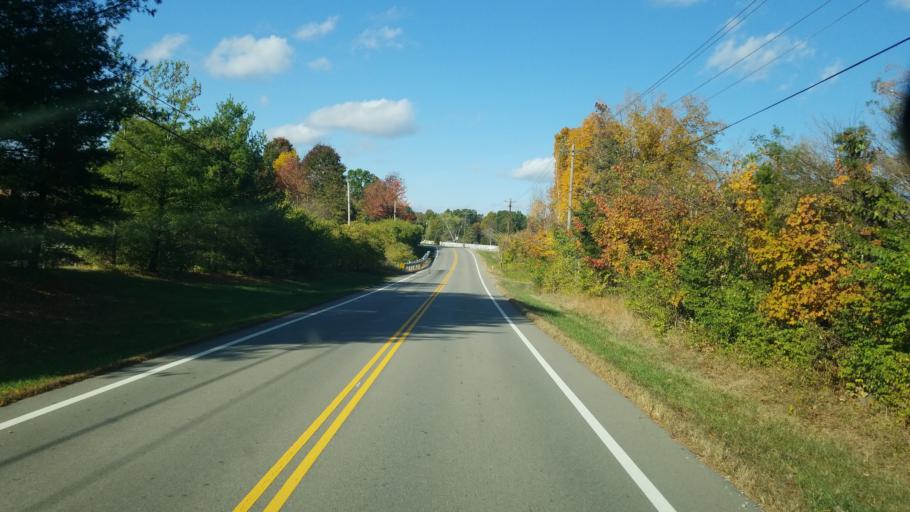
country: US
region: Ohio
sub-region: Warren County
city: Morrow
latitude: 39.4069
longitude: -84.1215
